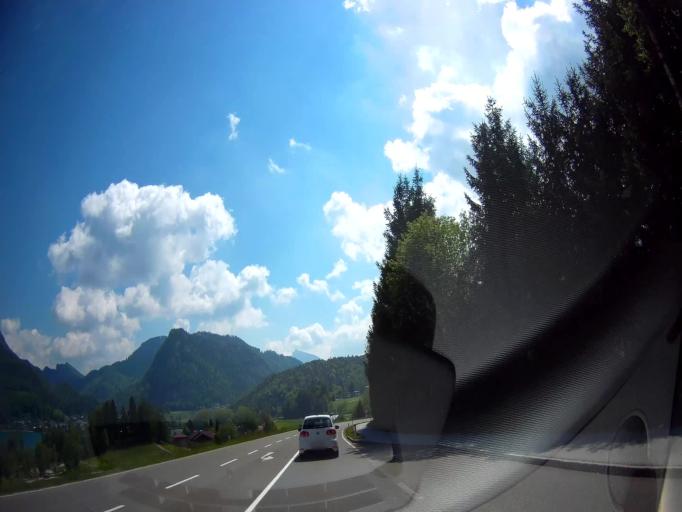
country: AT
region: Salzburg
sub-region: Politischer Bezirk Salzburg-Umgebung
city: Fuschl am See
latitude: 47.7918
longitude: 13.2864
